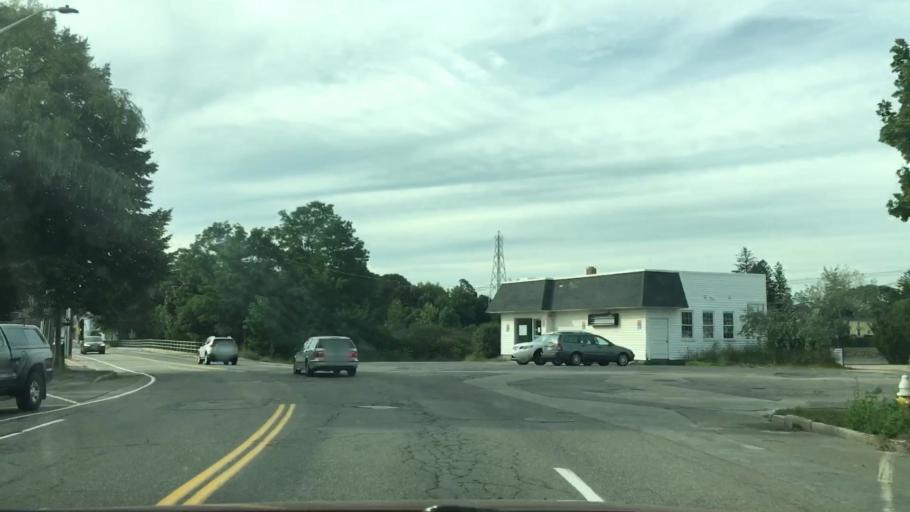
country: US
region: New Hampshire
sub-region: Rockingham County
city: Portsmouth
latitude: 43.0794
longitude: -70.7640
